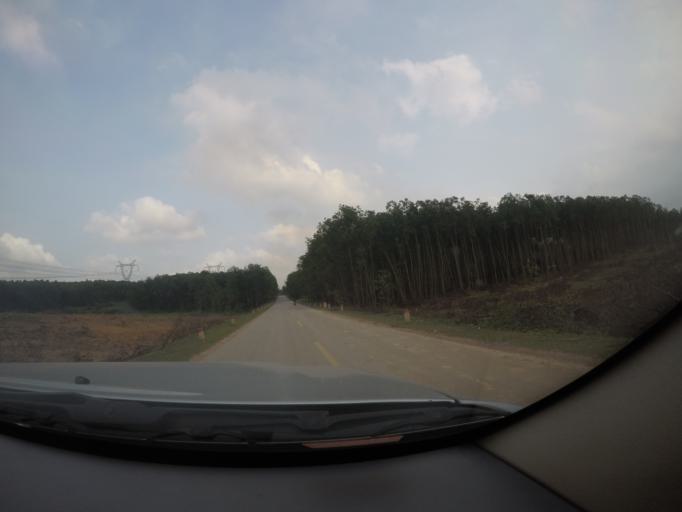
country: VN
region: Quang Binh
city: Kien Giang
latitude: 17.1169
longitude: 106.8049
